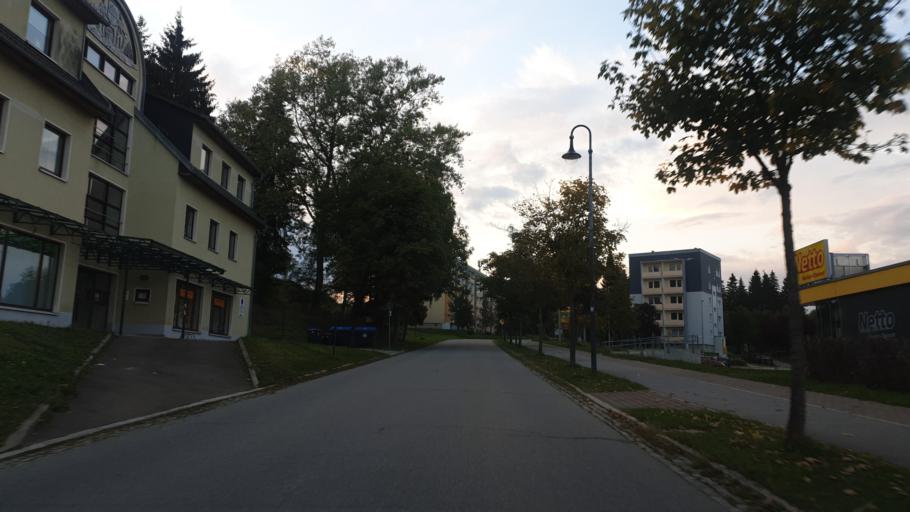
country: DE
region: Saxony
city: Johanngeorgenstadt
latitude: 50.4339
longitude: 12.7105
